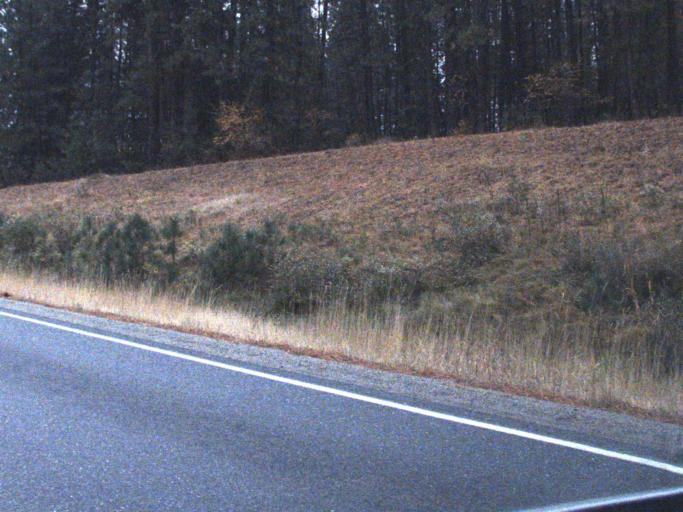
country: US
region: Washington
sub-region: Stevens County
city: Kettle Falls
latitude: 48.6157
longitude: -118.1035
